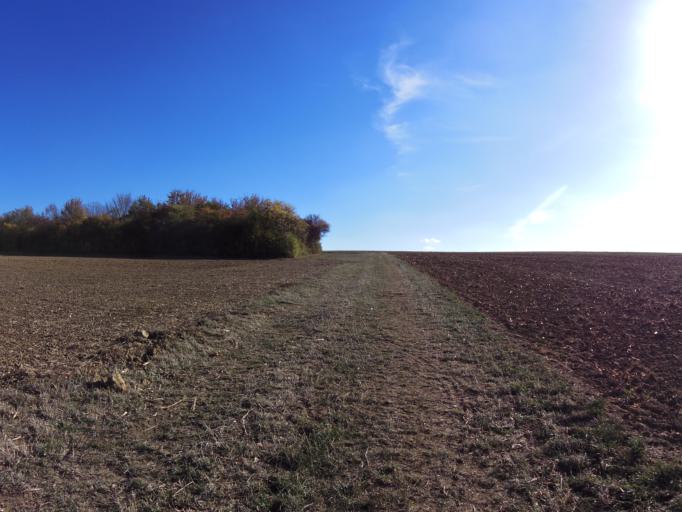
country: DE
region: Bavaria
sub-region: Regierungsbezirk Unterfranken
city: Reichenberg
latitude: 49.7027
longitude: 9.9357
